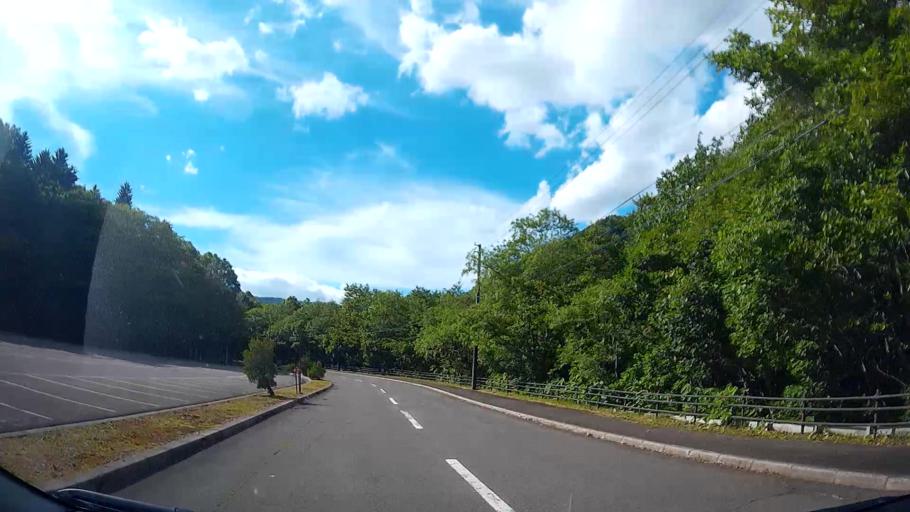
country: JP
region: Hokkaido
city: Sapporo
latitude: 42.9301
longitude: 141.1607
